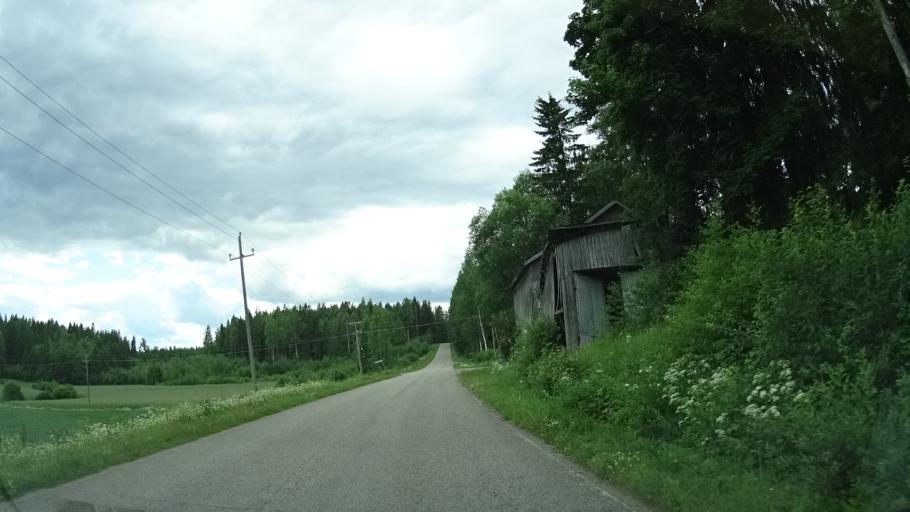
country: FI
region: Uusimaa
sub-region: Helsinki
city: Vihti
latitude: 60.4869
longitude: 24.4436
